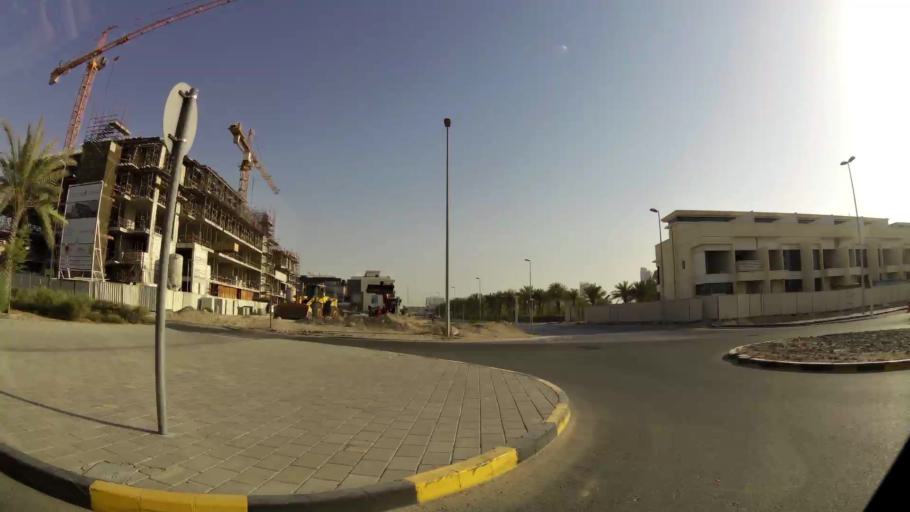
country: AE
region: Dubai
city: Dubai
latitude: 25.0504
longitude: 55.2039
